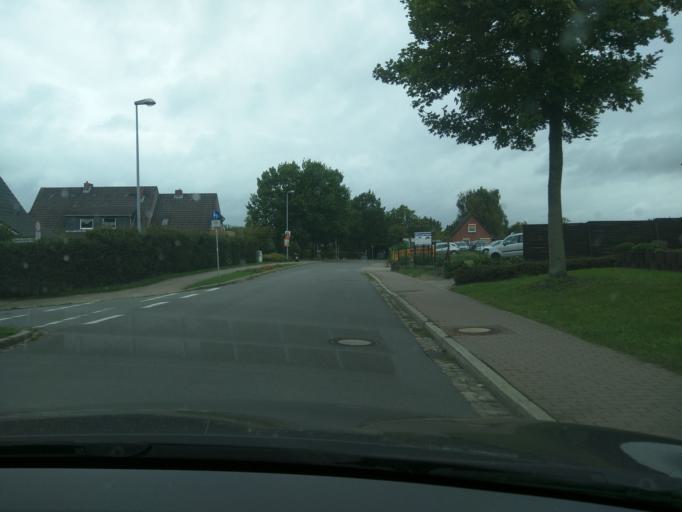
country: DE
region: Schleswig-Holstein
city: Lauenburg
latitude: 53.3819
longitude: 10.5536
